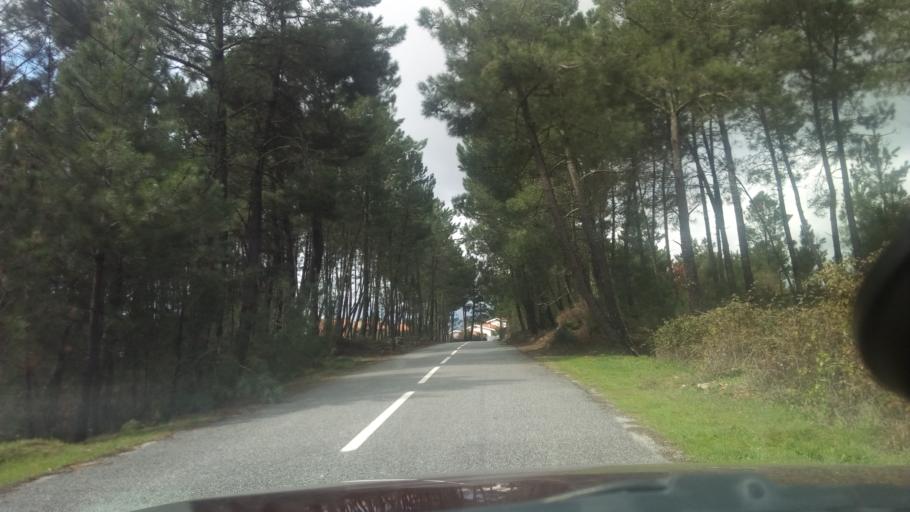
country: PT
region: Guarda
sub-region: Fornos de Algodres
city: Fornos de Algodres
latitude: 40.6043
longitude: -7.5041
